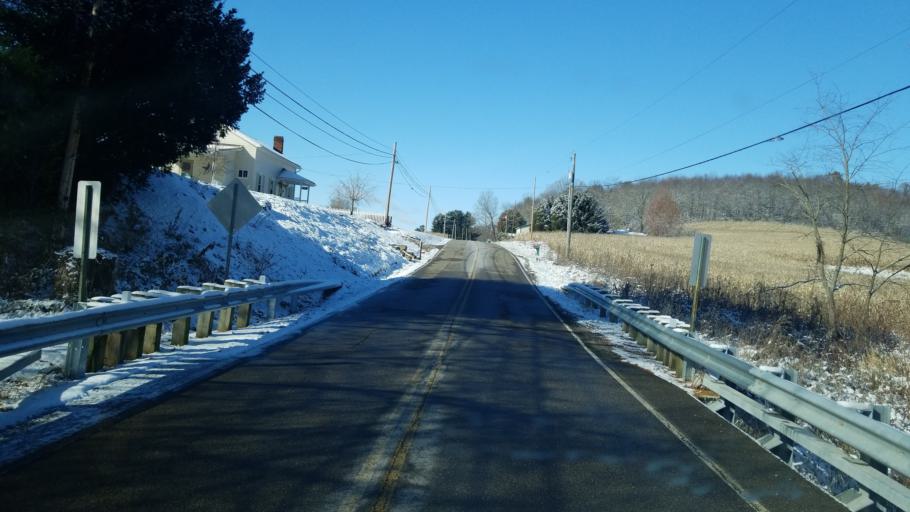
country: US
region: Ohio
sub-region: Licking County
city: Newark
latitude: 40.1603
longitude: -82.3429
